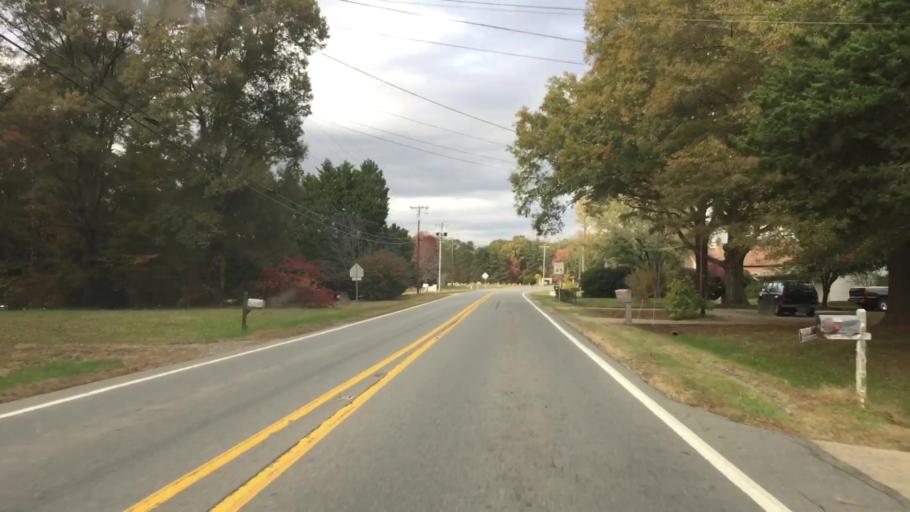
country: US
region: North Carolina
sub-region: Rockingham County
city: Reidsville
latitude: 36.3222
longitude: -79.7141
